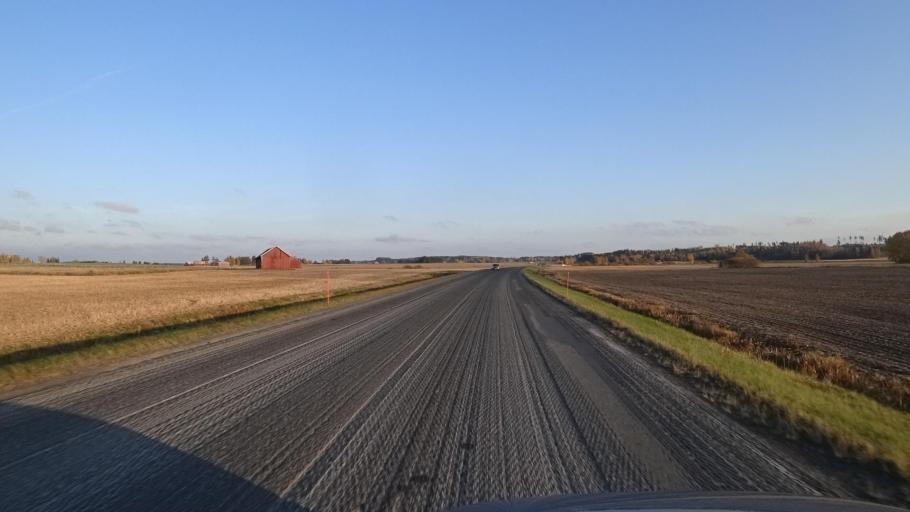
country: FI
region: Haeme
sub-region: Forssa
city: Ypaejae
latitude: 60.7938
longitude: 23.2812
